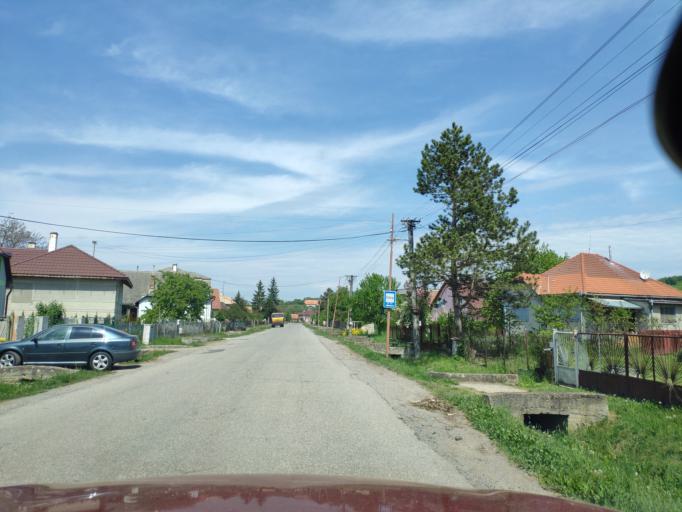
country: SK
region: Banskobystricky
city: Rimavska Sobota
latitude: 48.4417
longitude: 20.1148
